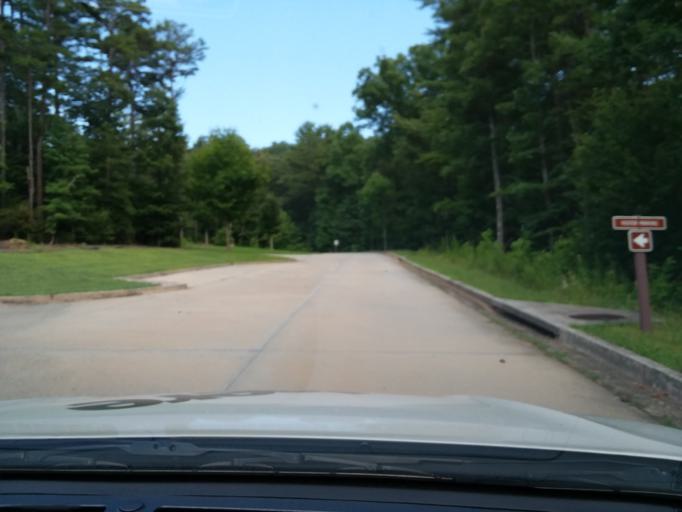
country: US
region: Georgia
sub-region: Rabun County
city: Clayton
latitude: 34.7527
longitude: -83.3965
